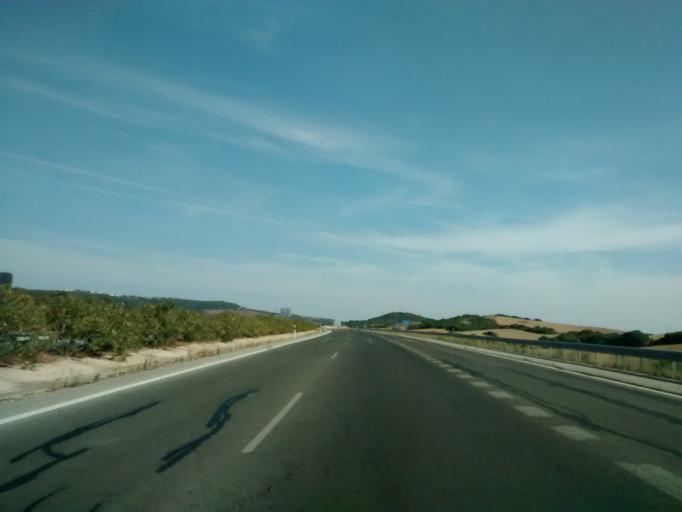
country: ES
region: Andalusia
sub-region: Provincia de Cadiz
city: Conil de la Frontera
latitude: 36.3014
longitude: -6.0560
